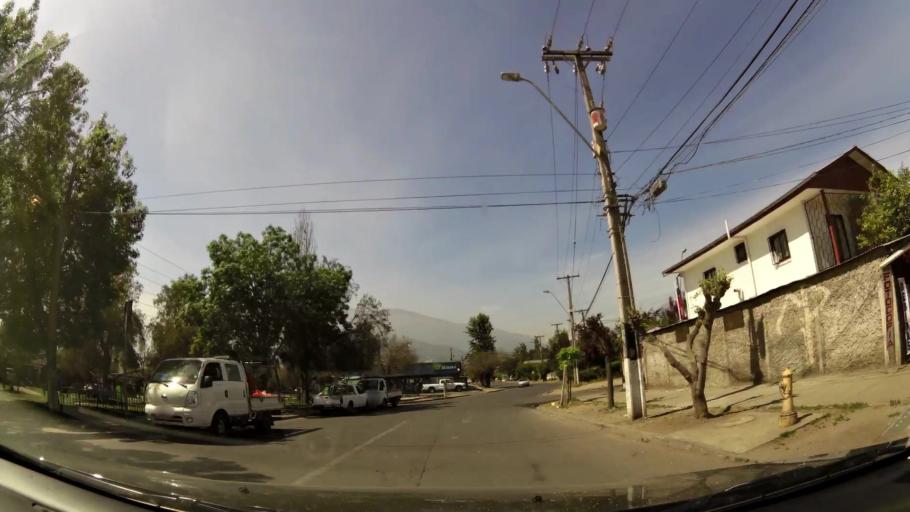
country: CL
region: Santiago Metropolitan
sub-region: Provincia de Cordillera
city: Puente Alto
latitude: -33.5711
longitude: -70.5766
